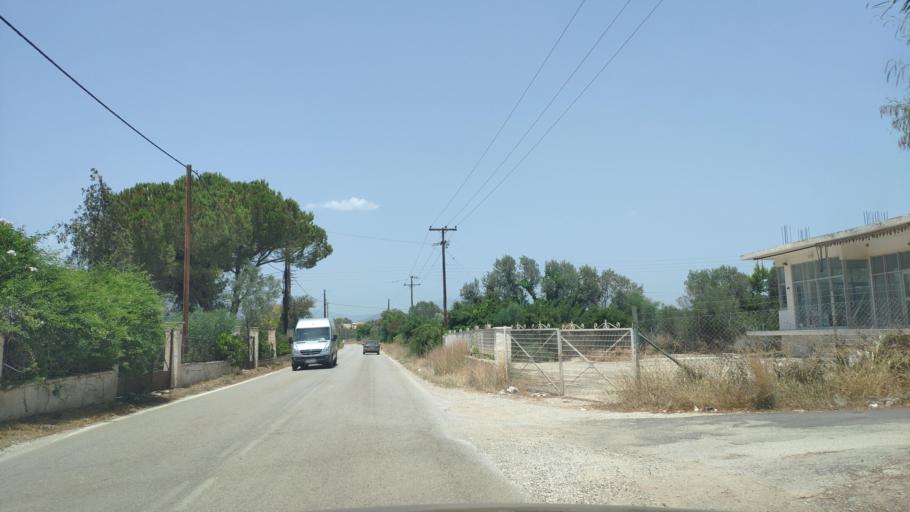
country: GR
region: Peloponnese
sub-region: Nomos Argolidos
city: Porto Cheli
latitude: 37.3131
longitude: 23.1582
